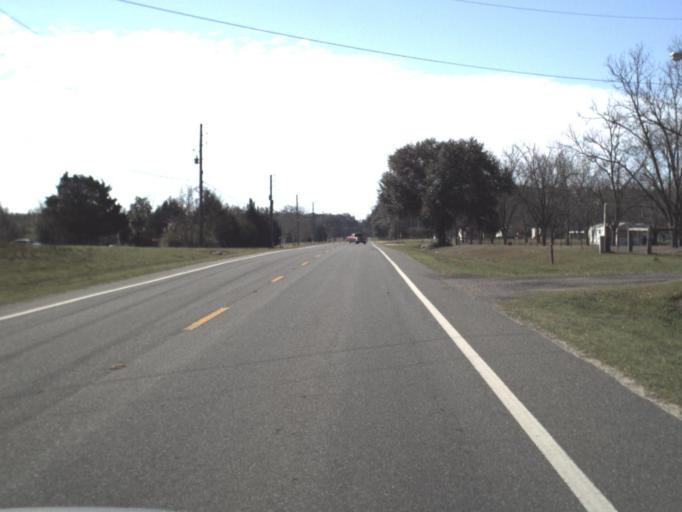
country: US
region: Florida
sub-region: Jackson County
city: Malone
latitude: 30.8880
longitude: -85.1613
